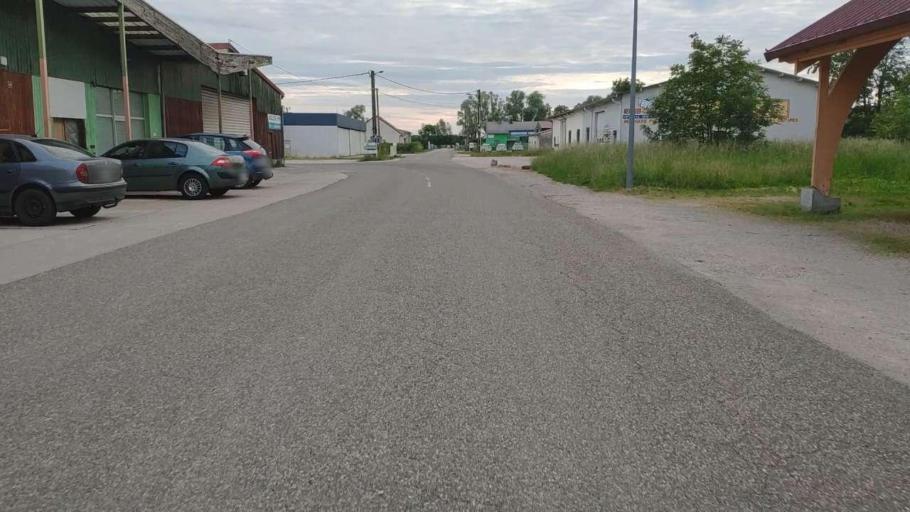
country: FR
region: Franche-Comte
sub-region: Departement du Jura
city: Bletterans
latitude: 46.7489
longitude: 5.4640
